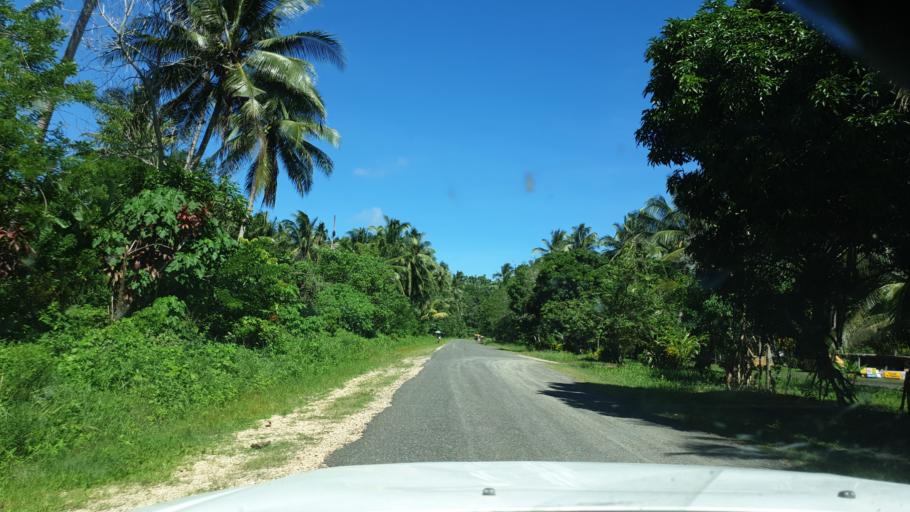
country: PG
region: Madang
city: Madang
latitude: -4.5261
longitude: 145.4719
